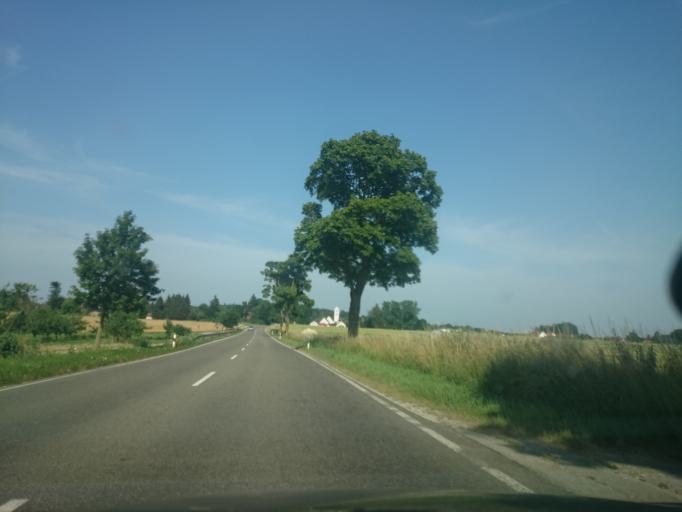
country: DE
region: Bavaria
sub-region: Upper Bavaria
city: Althegnenberg
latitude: 48.2329
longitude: 11.0545
